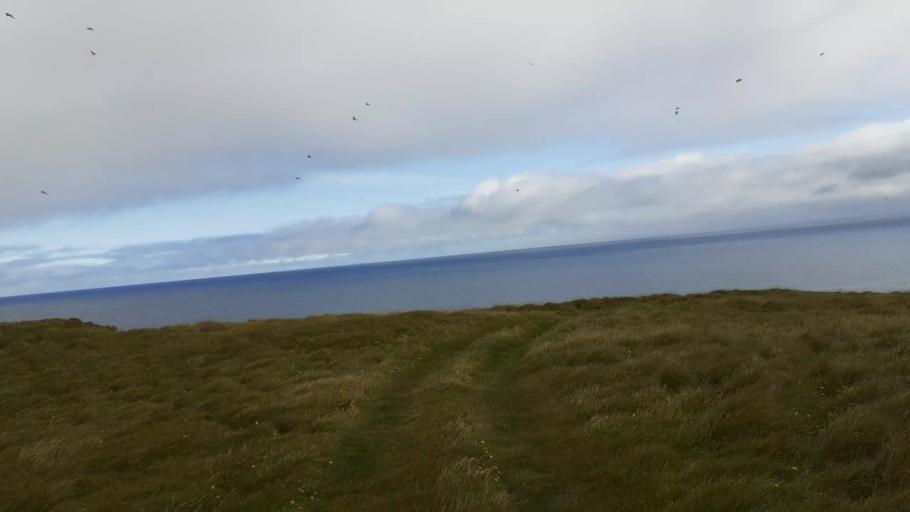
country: IS
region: Northeast
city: Dalvik
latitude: 66.5321
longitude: -17.9823
